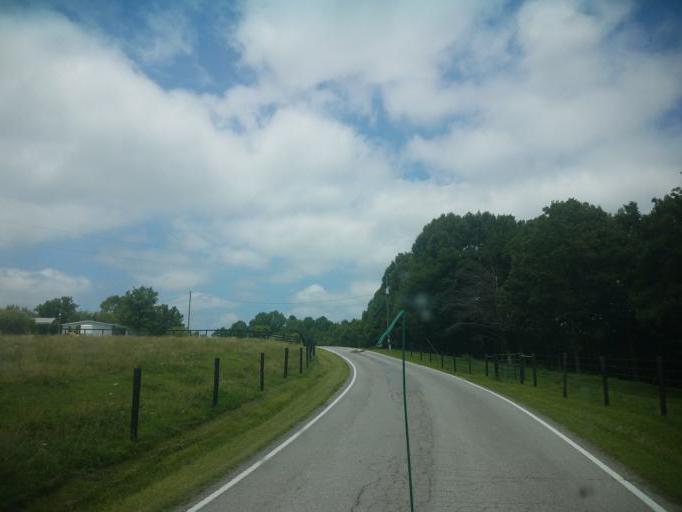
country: US
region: Kentucky
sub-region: Hart County
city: Munfordville
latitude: 37.3495
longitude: -86.0368
